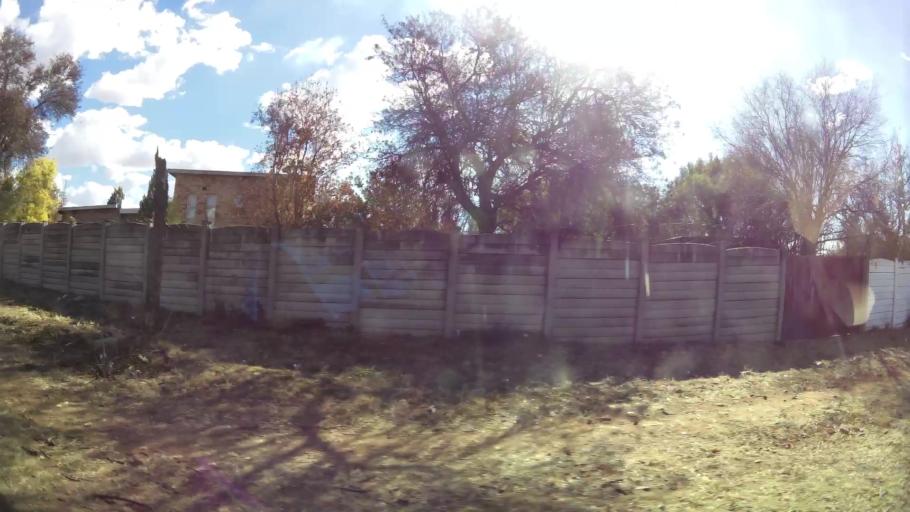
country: ZA
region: North-West
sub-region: Dr Kenneth Kaunda District Municipality
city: Klerksdorp
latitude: -26.8540
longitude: 26.6462
